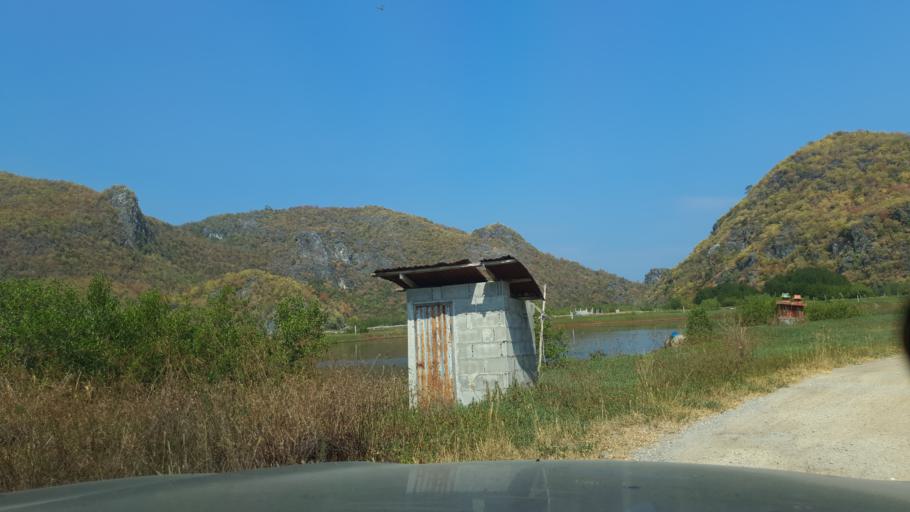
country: TH
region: Prachuap Khiri Khan
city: Sam Roi Yot
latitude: 12.1976
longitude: 99.9913
